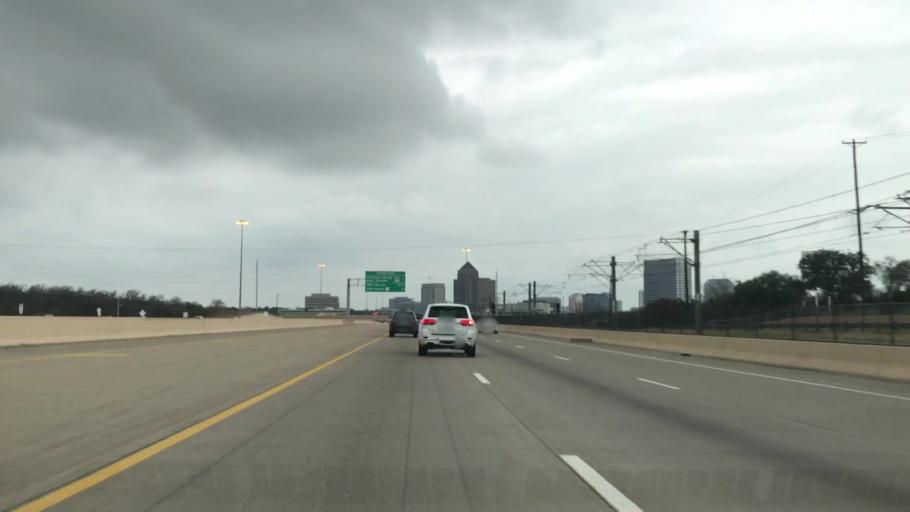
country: US
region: Texas
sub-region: Dallas County
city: Irving
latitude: 32.8520
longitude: -96.9213
